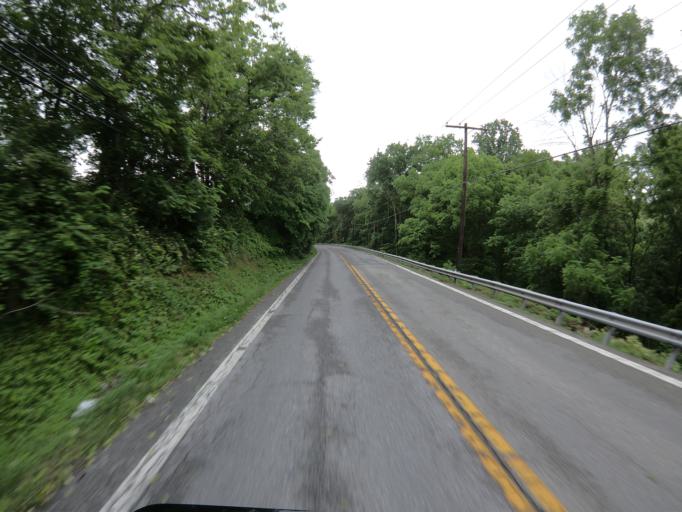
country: US
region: Maryland
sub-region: Frederick County
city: Middletown
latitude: 39.4572
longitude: -77.5771
